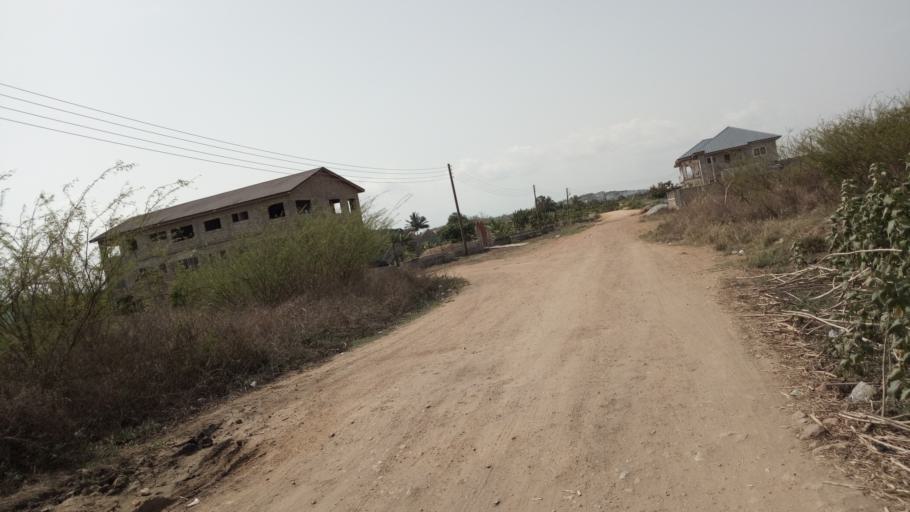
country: GH
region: Central
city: Winneba
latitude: 5.3709
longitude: -0.6485
